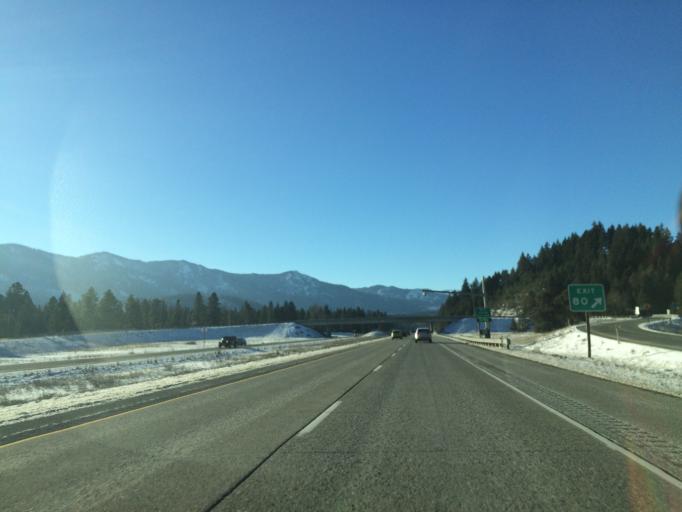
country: US
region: Washington
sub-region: Kittitas County
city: Cle Elum
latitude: 47.1841
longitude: -121.0112
